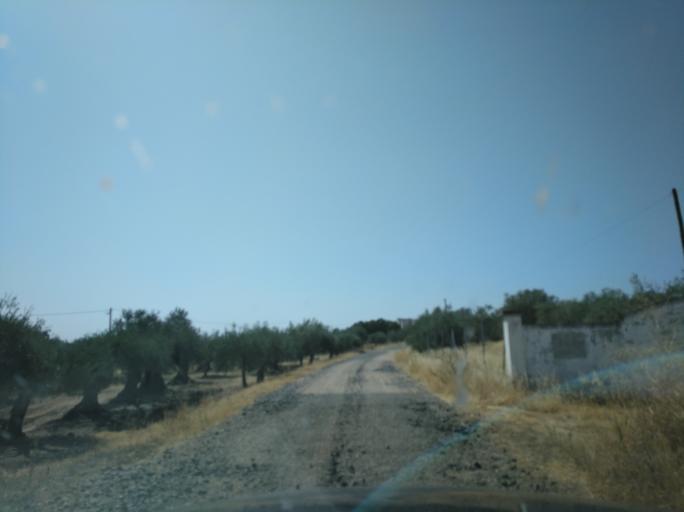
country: PT
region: Portalegre
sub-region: Campo Maior
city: Campo Maior
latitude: 39.0731
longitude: -7.0170
